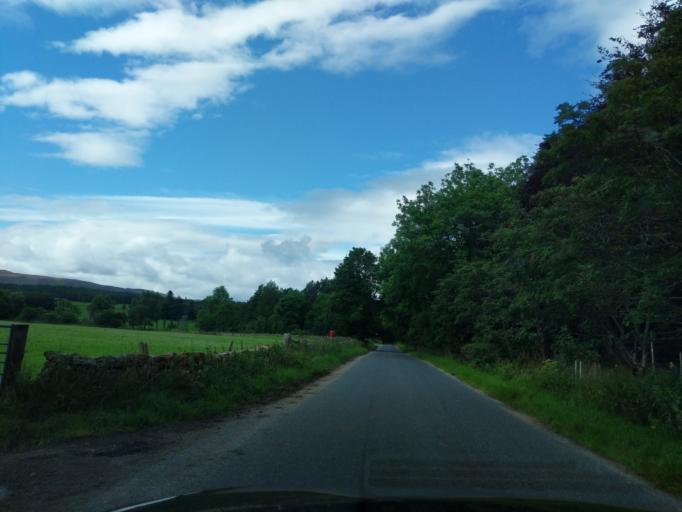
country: GB
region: Scotland
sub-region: Aberdeenshire
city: Ballater
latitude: 57.0420
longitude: -3.1755
